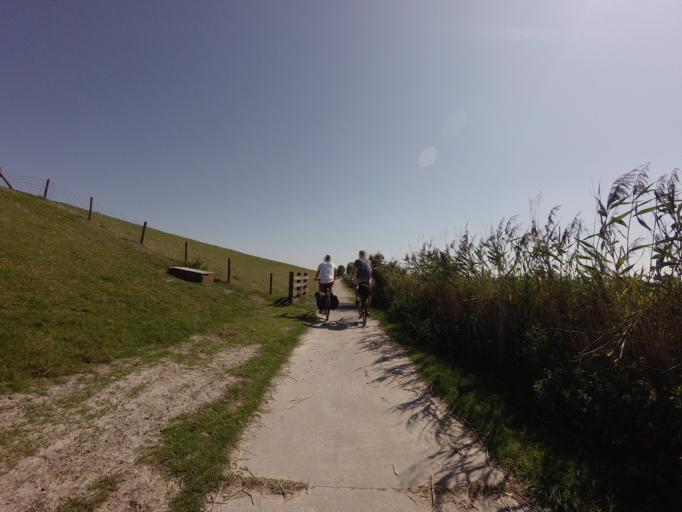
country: NL
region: Friesland
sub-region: Gemeente Dongeradeel
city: Anjum
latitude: 53.3987
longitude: 6.1017
